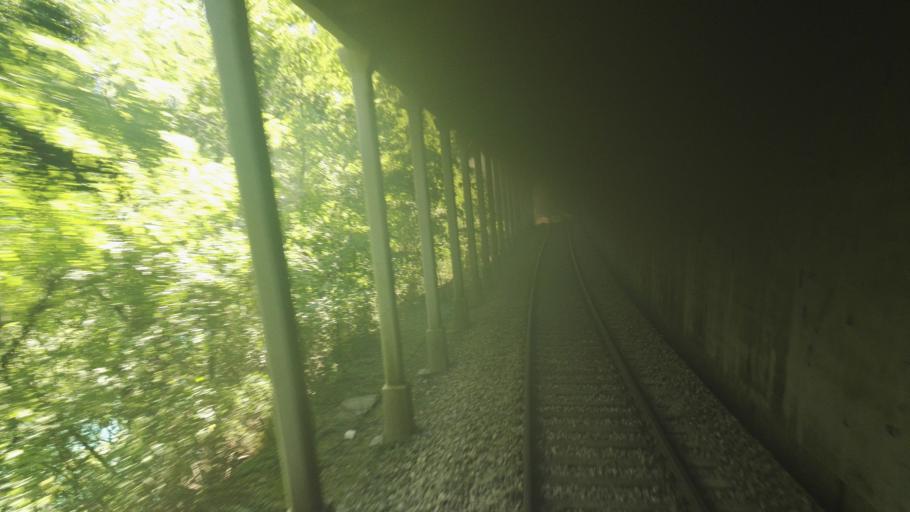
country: SI
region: Kanal
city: Kanal
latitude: 46.1044
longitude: 13.6788
